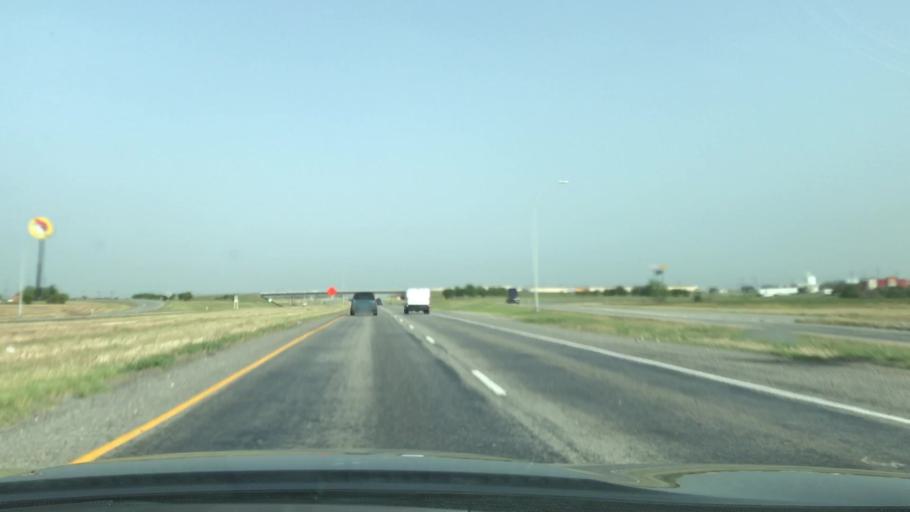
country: US
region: Texas
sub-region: Kaufman County
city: Terrell
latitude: 32.7191
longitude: -96.3152
